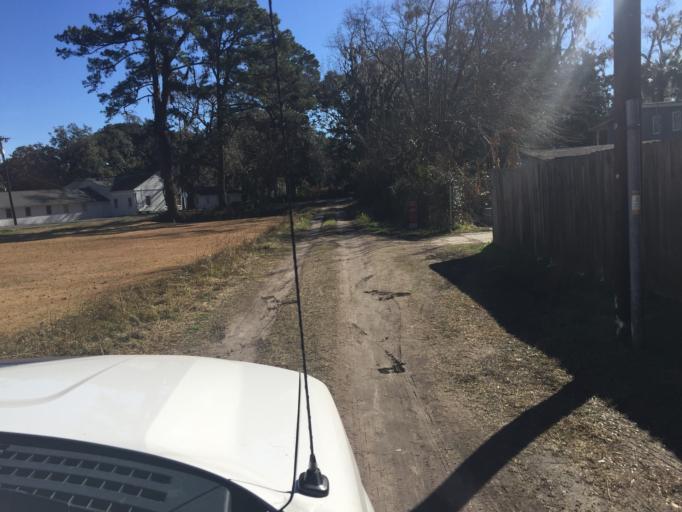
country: US
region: Georgia
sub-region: Chatham County
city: Thunderbolt
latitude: 32.0125
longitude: -81.0661
